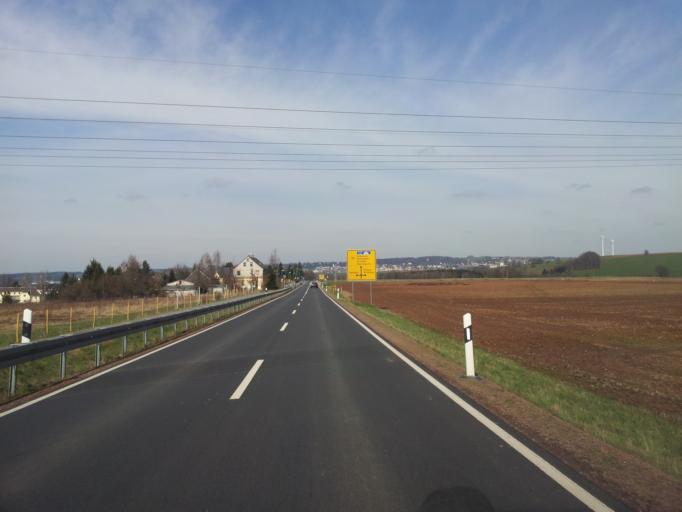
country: DE
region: Saxony
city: Gersdorf
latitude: 50.7571
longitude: 12.7192
